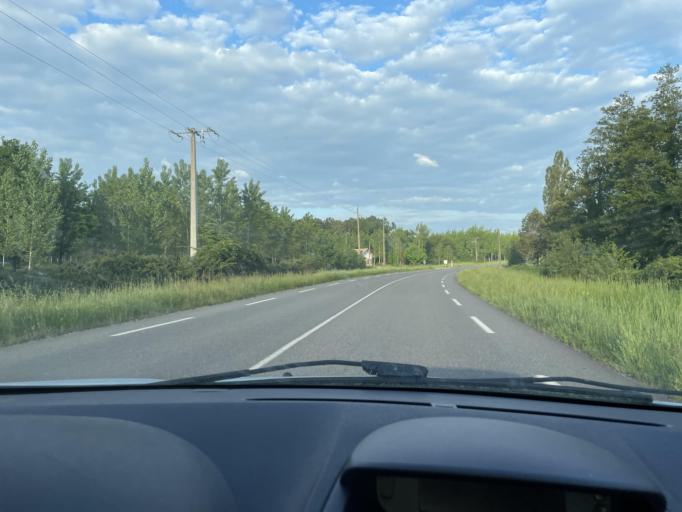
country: FR
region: Aquitaine
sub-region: Departement de la Gironde
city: Grignols
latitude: 44.3941
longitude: -0.0577
